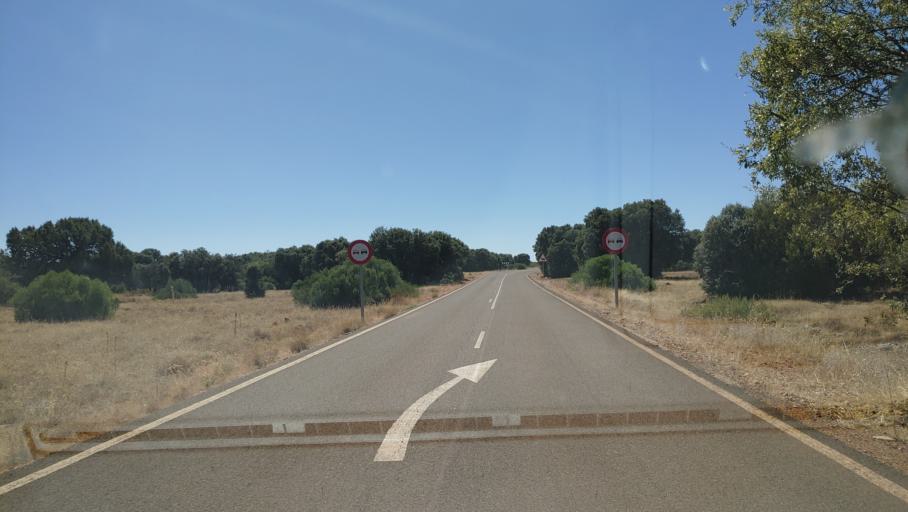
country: ES
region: Castille-La Mancha
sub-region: Provincia de Ciudad Real
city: Villahermosa
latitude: 38.8360
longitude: -2.8193
